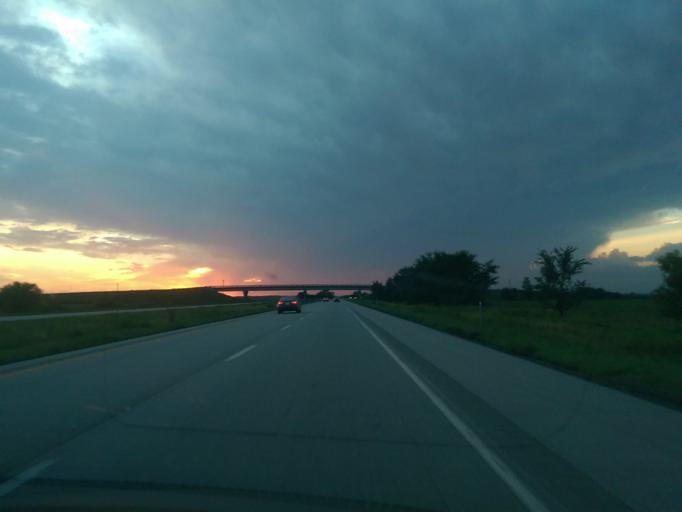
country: US
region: Iowa
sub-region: Fremont County
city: Hamburg
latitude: 40.6384
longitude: -95.7333
